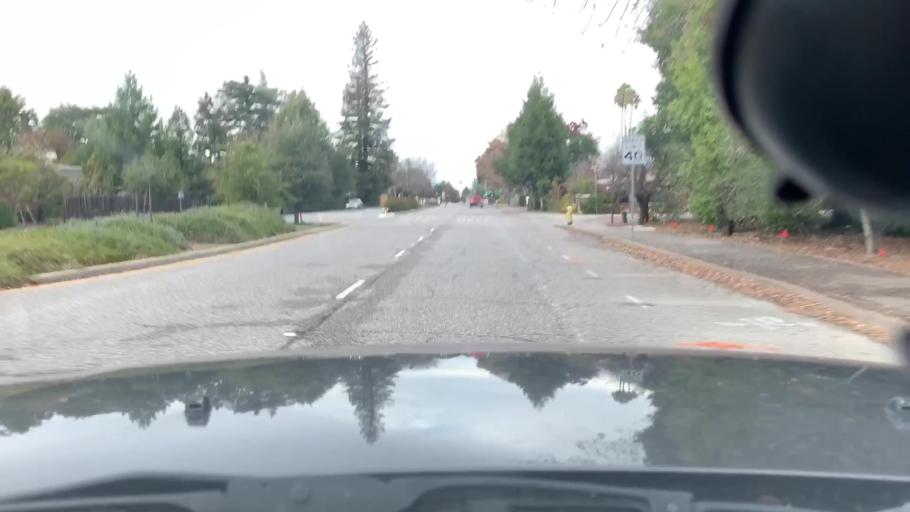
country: US
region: California
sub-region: Santa Clara County
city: Saratoga
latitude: 37.2627
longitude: -122.0319
